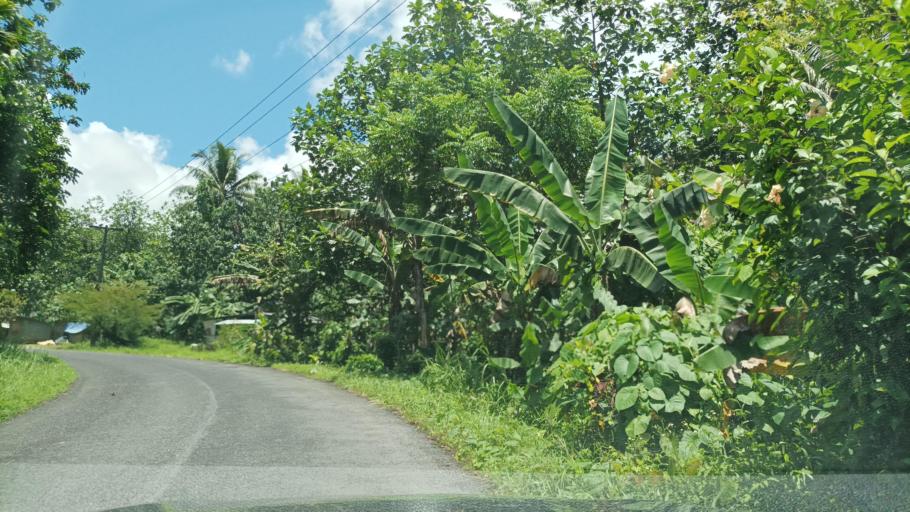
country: FM
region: Pohnpei
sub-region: Madolenihm Municipality
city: Madolenihm Municipality Government
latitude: 6.8735
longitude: 158.2859
